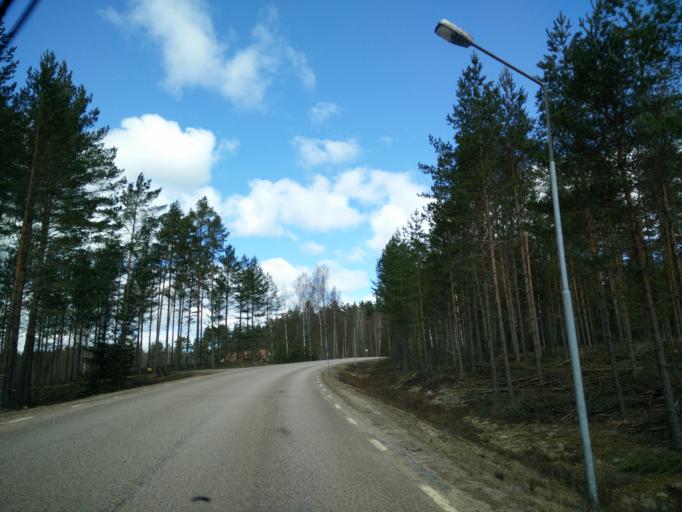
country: SE
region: Vaermland
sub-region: Hagfors Kommun
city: Hagfors
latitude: 59.8854
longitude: 13.7134
